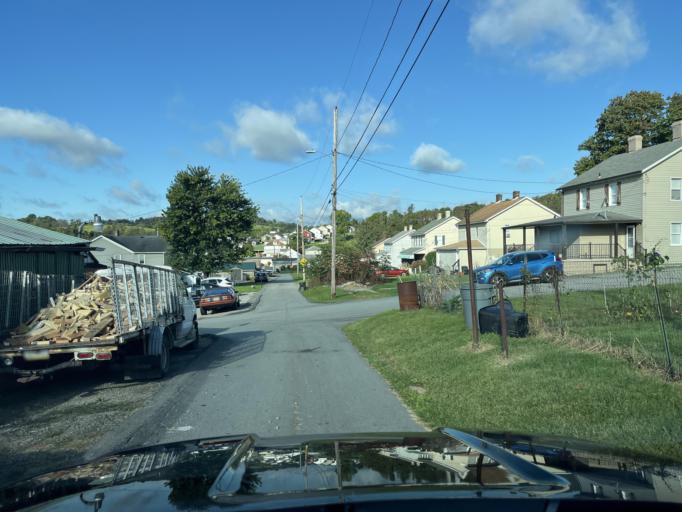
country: US
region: Pennsylvania
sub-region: Fayette County
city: South Uniontown
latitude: 39.8788
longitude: -79.7655
